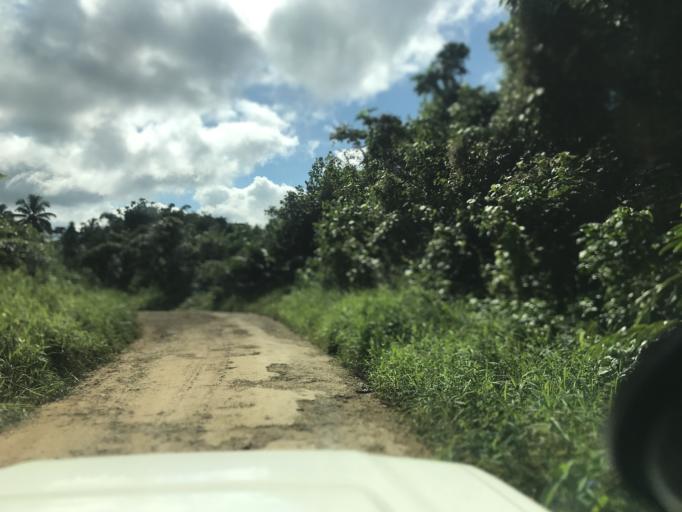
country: VU
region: Sanma
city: Luganville
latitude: -15.4656
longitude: 167.0711
